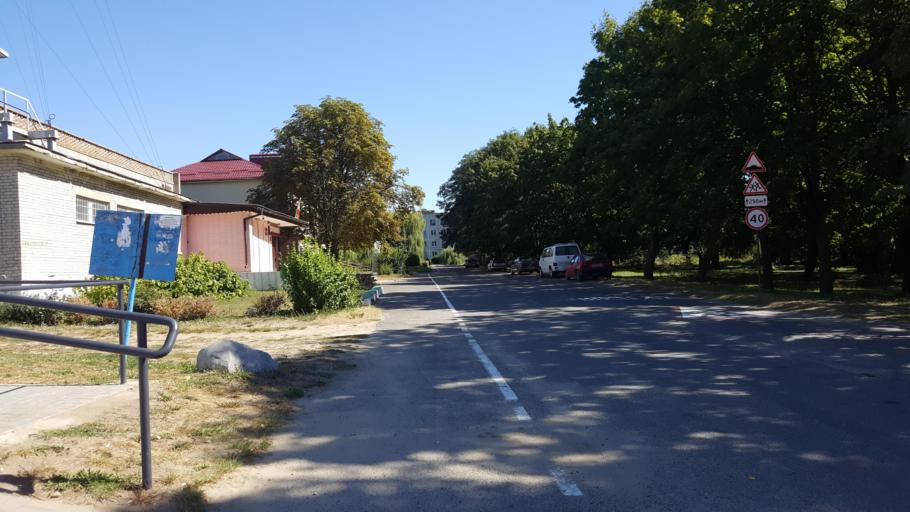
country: BY
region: Brest
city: Vysokaye
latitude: 52.2219
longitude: 23.4513
